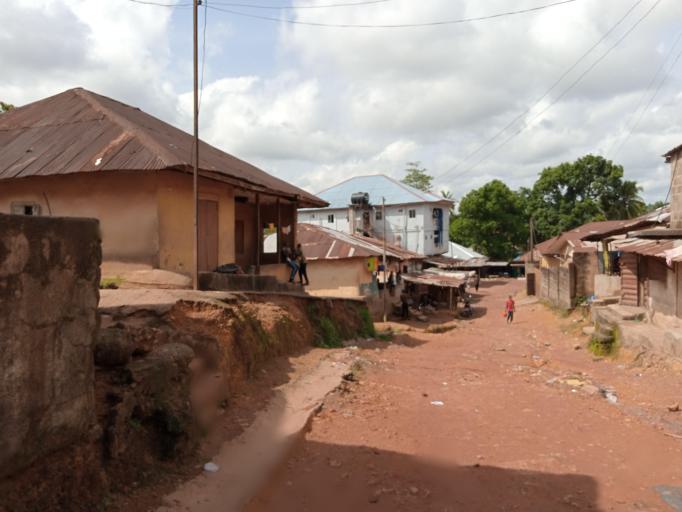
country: SL
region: Southern Province
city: Bo
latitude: 7.9620
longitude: -11.7356
